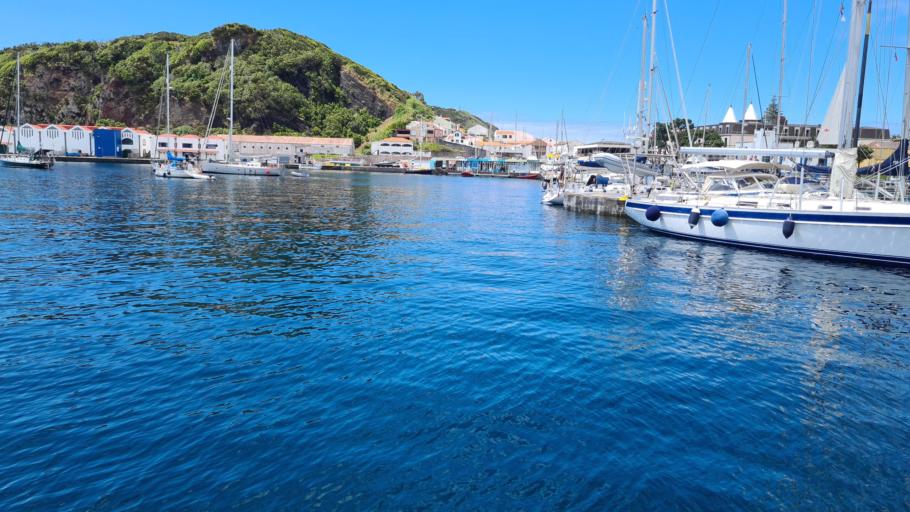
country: PT
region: Azores
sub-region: Horta
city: Horta
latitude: 38.5302
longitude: -28.6250
